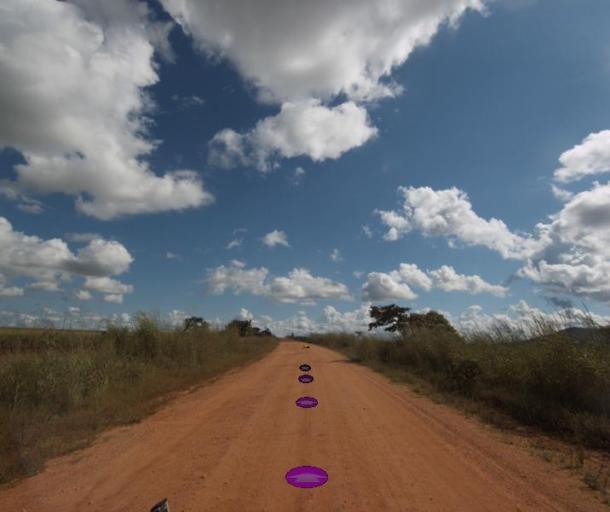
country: BR
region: Goias
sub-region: Jaragua
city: Jaragua
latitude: -15.8255
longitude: -49.2330
